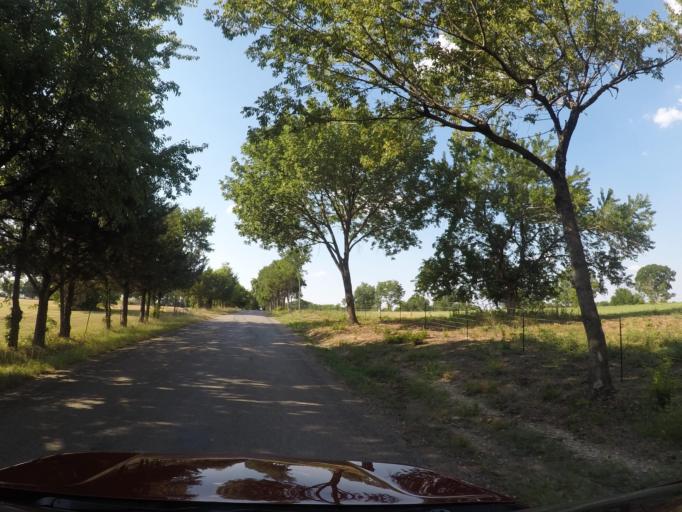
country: US
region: Texas
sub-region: Grayson County
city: Pottsboro
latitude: 33.8001
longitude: -96.6068
